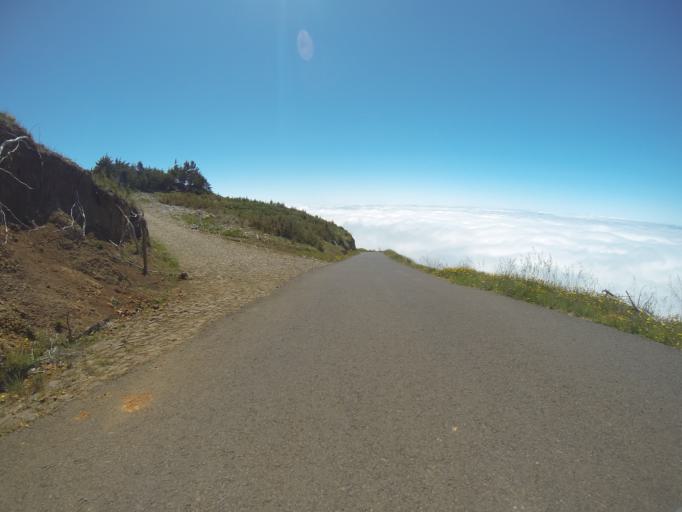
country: PT
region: Madeira
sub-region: Funchal
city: Nossa Senhora do Monte
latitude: 32.7051
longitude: -16.9146
